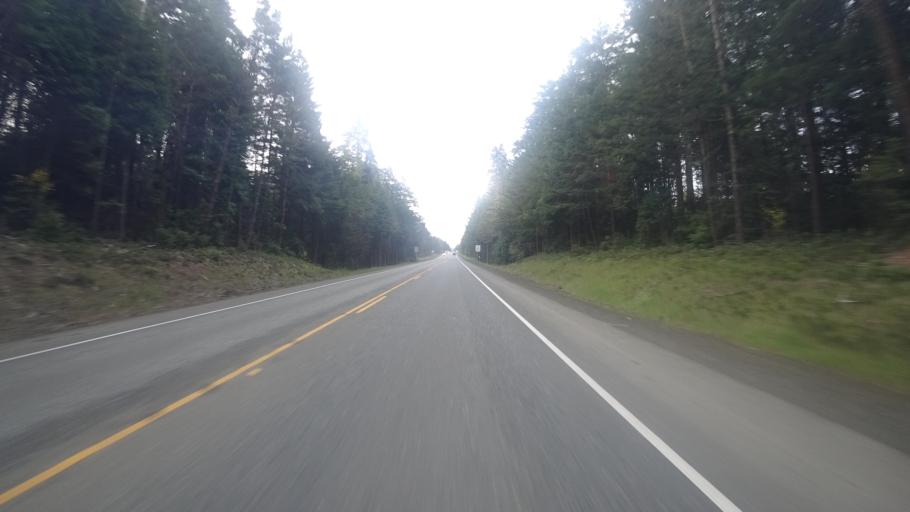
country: US
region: Oregon
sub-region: Coos County
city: Lakeside
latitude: 43.5198
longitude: -124.2167
